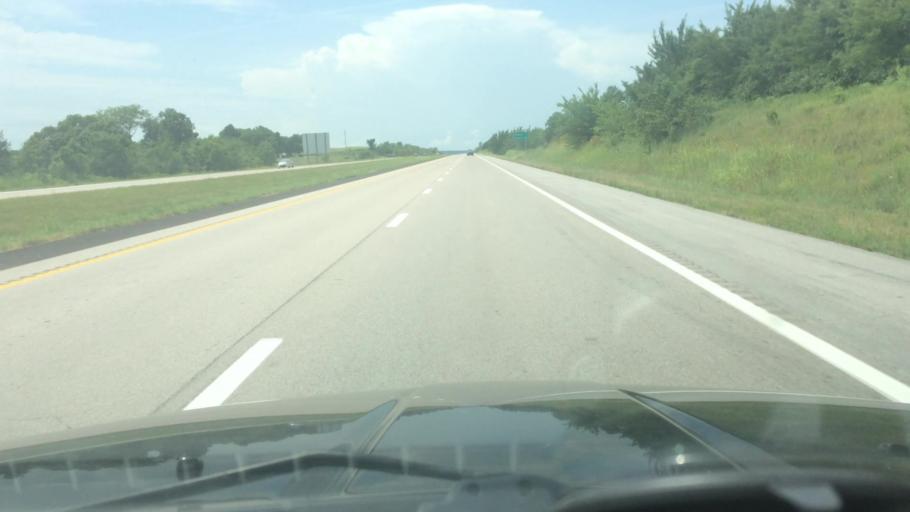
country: US
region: Missouri
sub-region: Polk County
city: Humansville
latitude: 37.7967
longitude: -93.5909
